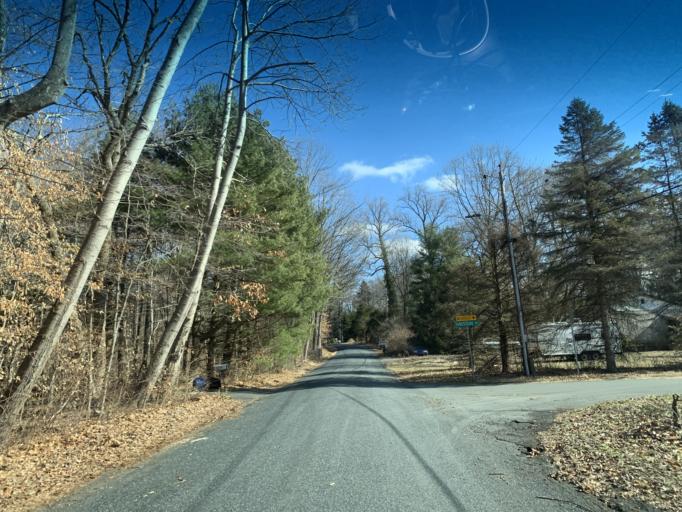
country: US
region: Maryland
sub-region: Harford County
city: Riverside
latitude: 39.5098
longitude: -76.2402
